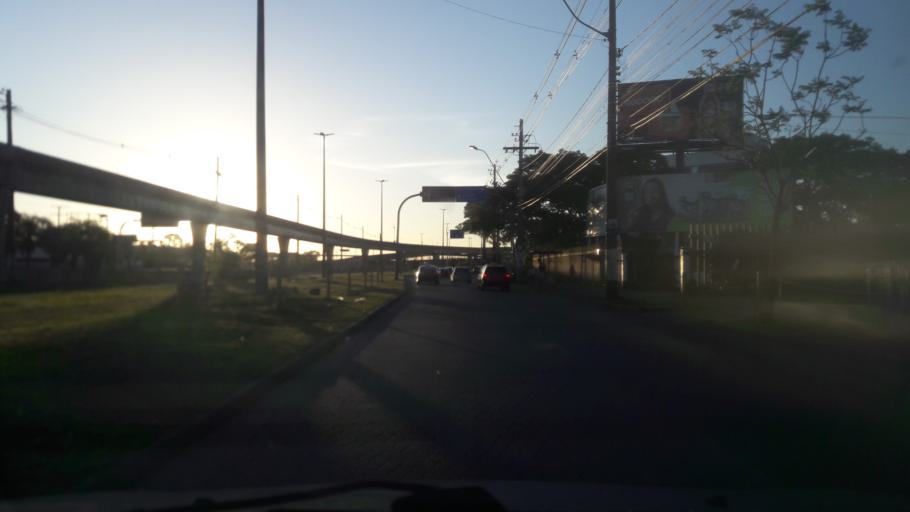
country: BR
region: Rio Grande do Sul
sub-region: Porto Alegre
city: Porto Alegre
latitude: -29.9882
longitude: -51.1777
